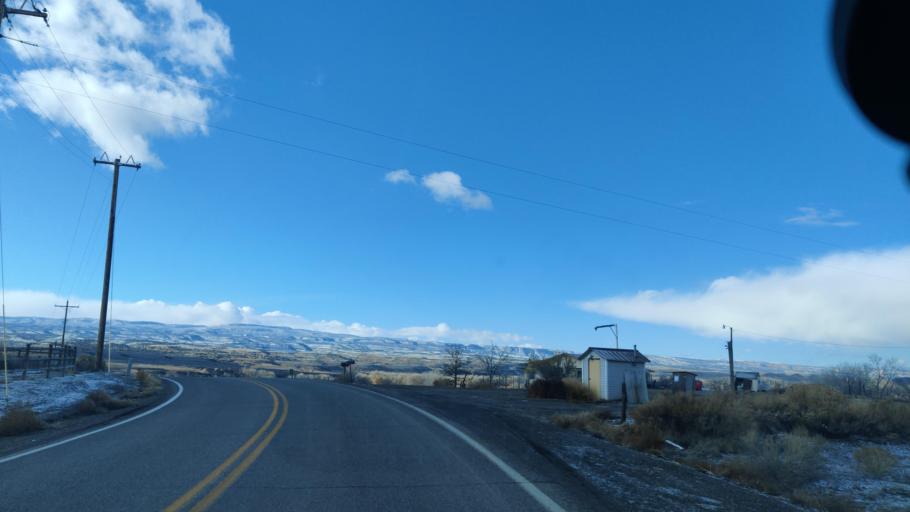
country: US
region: Colorado
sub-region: Mesa County
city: Clifton
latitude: 38.9887
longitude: -108.4429
